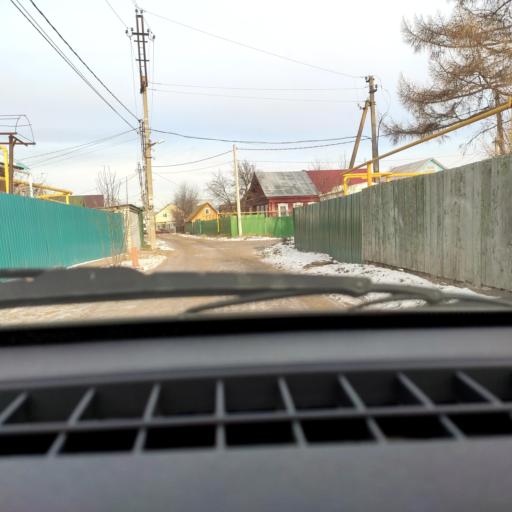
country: RU
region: Bashkortostan
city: Mikhaylovka
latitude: 54.7455
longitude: 55.9038
